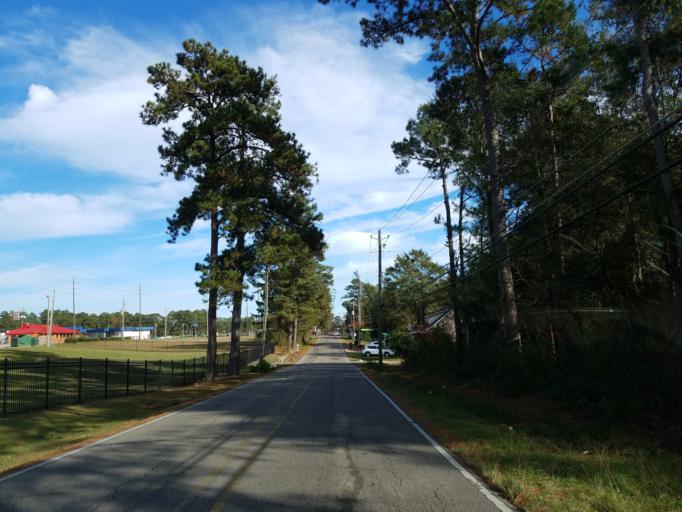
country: US
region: Mississippi
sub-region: Forrest County
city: Glendale
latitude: 31.3466
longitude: -89.3371
